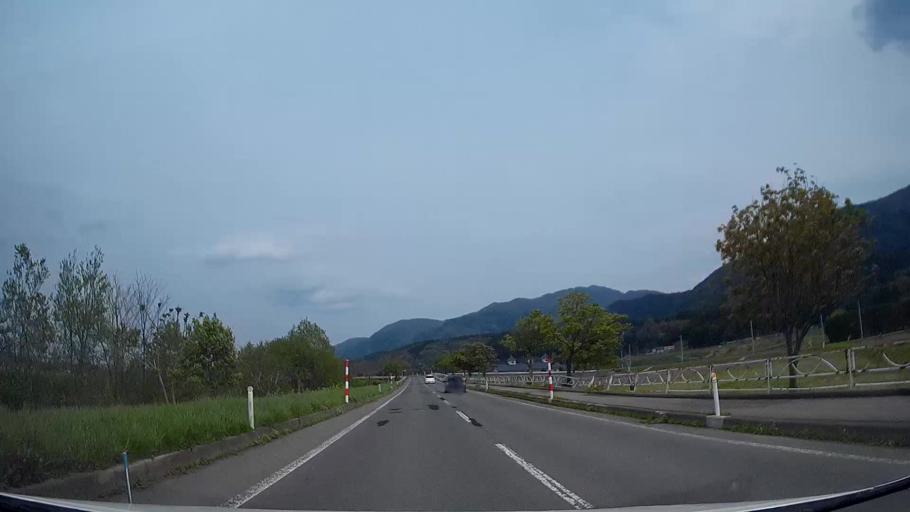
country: JP
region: Akita
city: Hanawa
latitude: 40.1177
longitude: 140.7820
